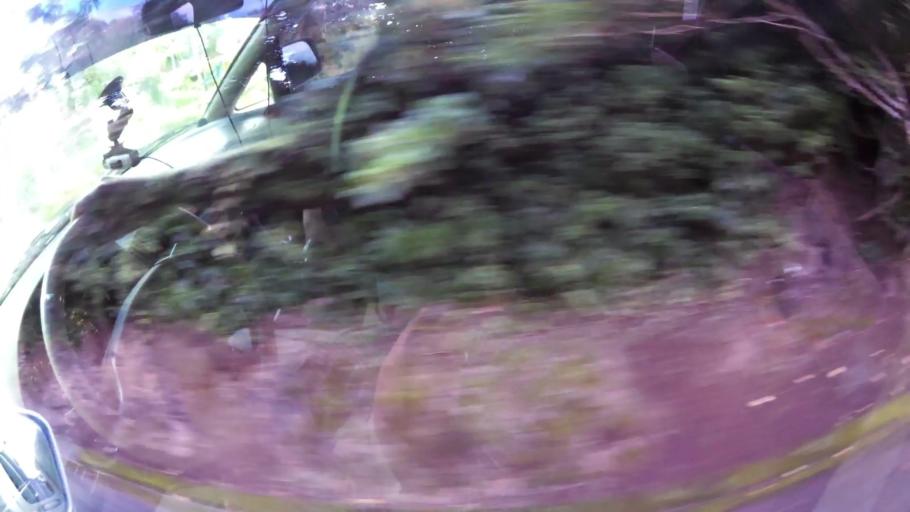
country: VC
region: Saint George
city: Kingstown
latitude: 13.1649
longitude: -61.1769
